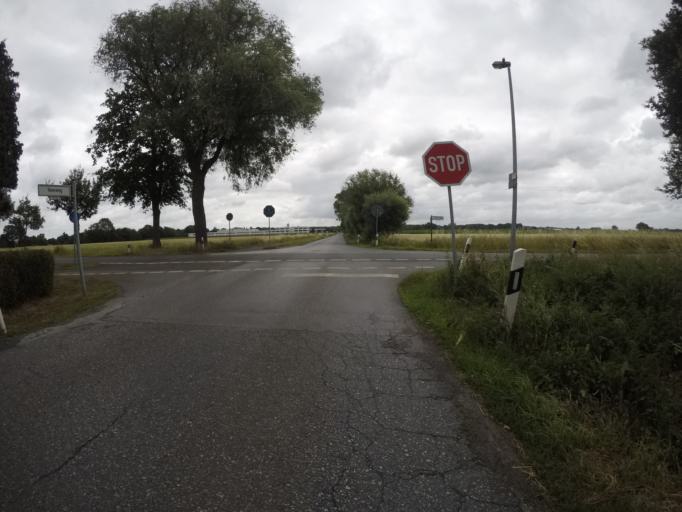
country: DE
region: North Rhine-Westphalia
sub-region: Regierungsbezirk Dusseldorf
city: Bocholt
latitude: 51.8084
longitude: 6.5959
